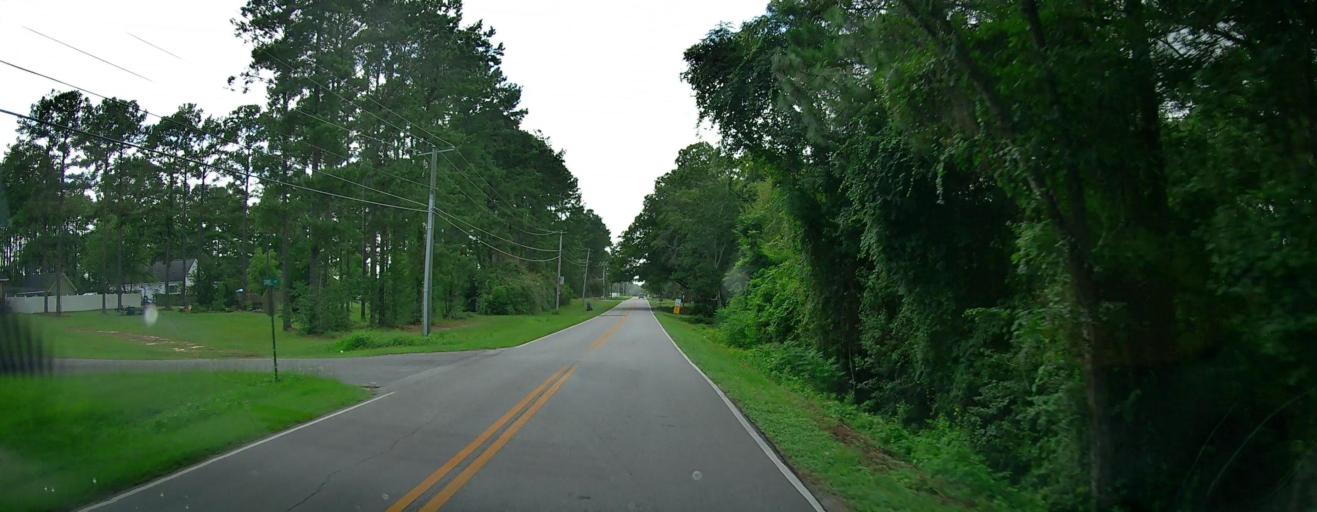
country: US
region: Georgia
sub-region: Ben Hill County
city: Fitzgerald
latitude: 31.7056
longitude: -83.2837
